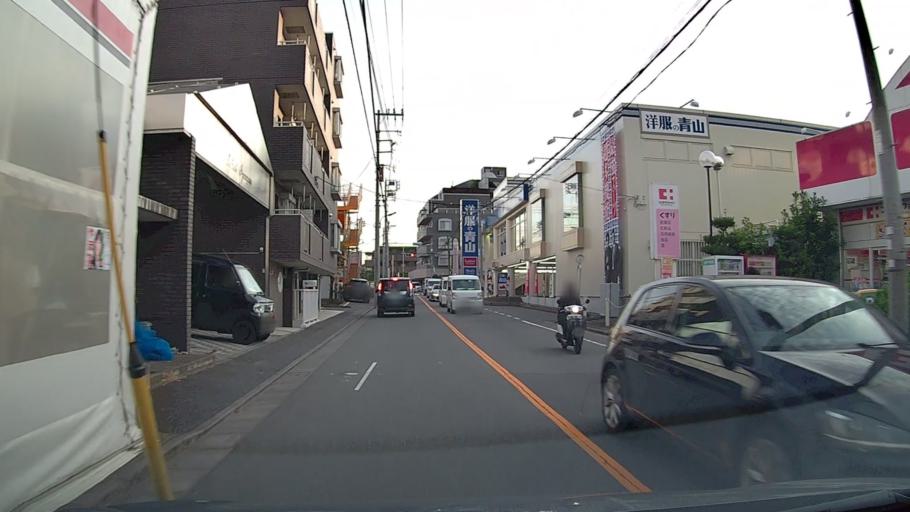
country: JP
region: Saitama
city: Wako
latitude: 35.7604
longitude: 139.6356
